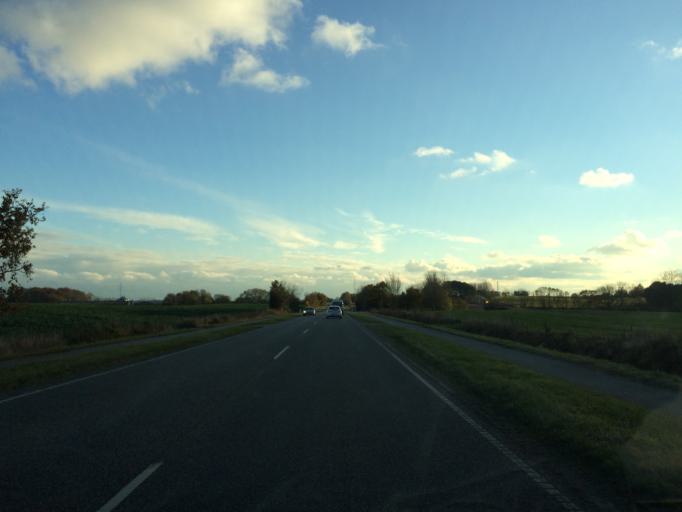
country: DK
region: South Denmark
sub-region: Sonderborg Kommune
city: Guderup
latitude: 55.0153
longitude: 9.8461
